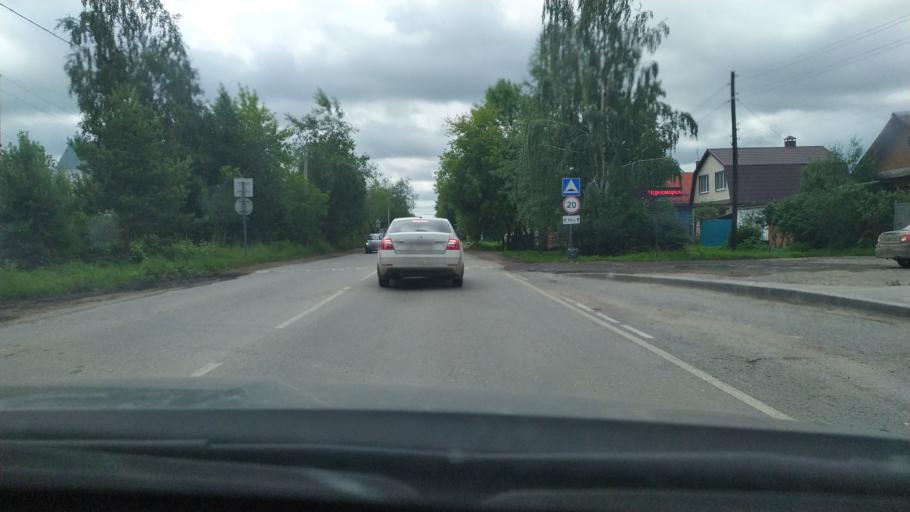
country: RU
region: Perm
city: Perm
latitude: 57.9816
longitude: 56.3048
